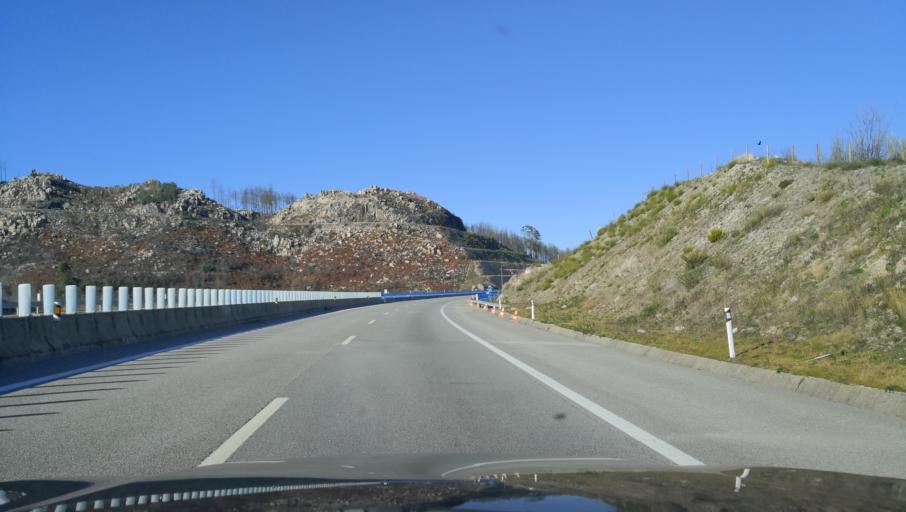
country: PT
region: Viseu
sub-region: Vouzela
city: Vouzela
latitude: 40.6863
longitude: -8.0779
